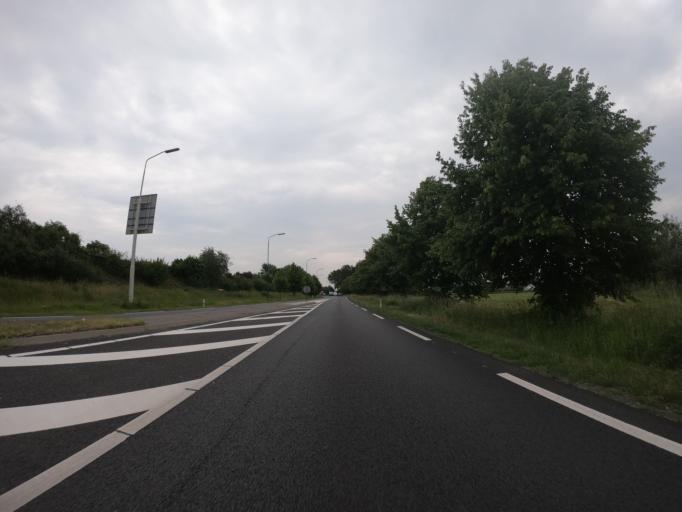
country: NL
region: North Brabant
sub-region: Gemeente Uden
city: Uden
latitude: 51.6503
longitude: 5.6045
